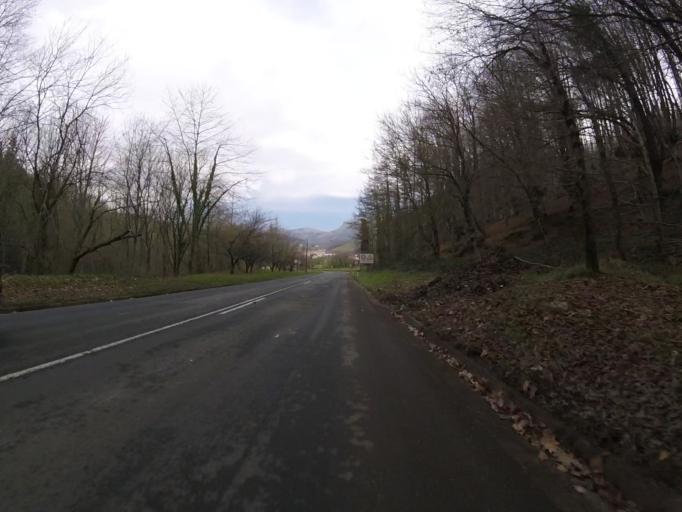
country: ES
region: Basque Country
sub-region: Provincia de Guipuzcoa
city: Albiztur
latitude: 43.1266
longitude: -2.1582
